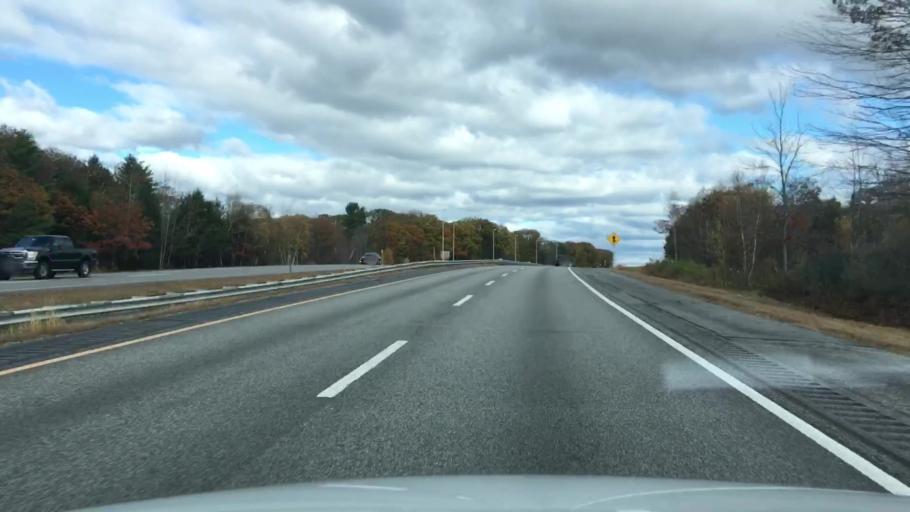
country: US
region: Maine
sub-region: Cumberland County
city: Freeport
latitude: 43.8440
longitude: -70.1204
